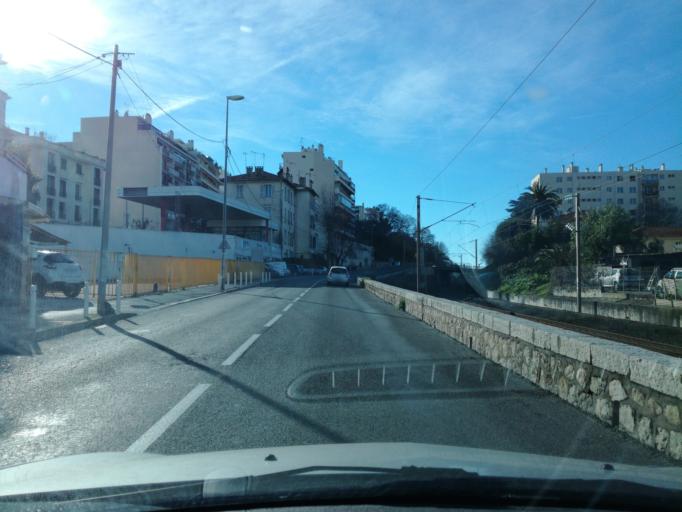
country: FR
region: Provence-Alpes-Cote d'Azur
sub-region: Departement des Alpes-Maritimes
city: Antibes
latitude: 43.5771
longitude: 7.1173
